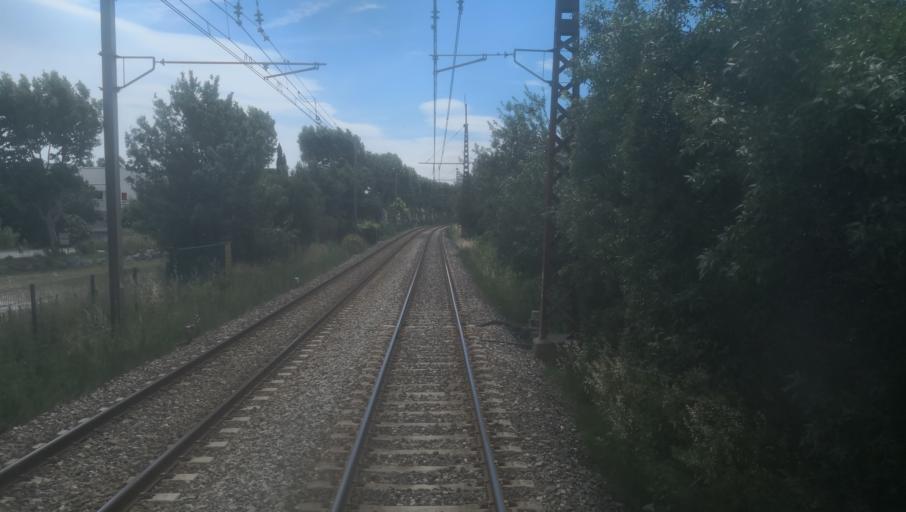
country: FR
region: Languedoc-Roussillon
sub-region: Departement de l'Aude
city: Narbonne
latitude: 43.1981
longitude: 3.0144
